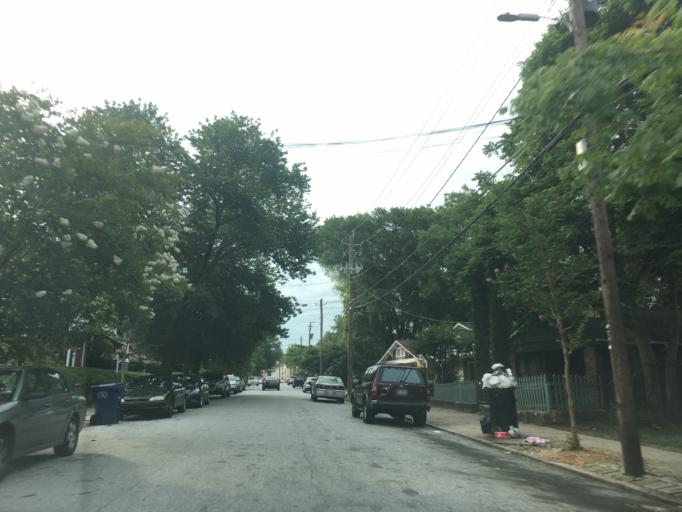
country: US
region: Georgia
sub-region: Fulton County
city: Atlanta
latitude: 33.7669
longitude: -84.3766
